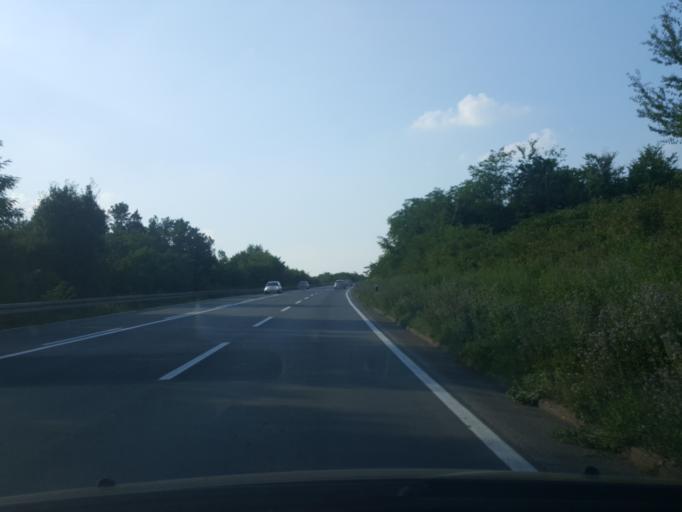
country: RS
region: Central Serbia
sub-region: Belgrade
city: Sopot
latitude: 44.5096
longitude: 20.6541
